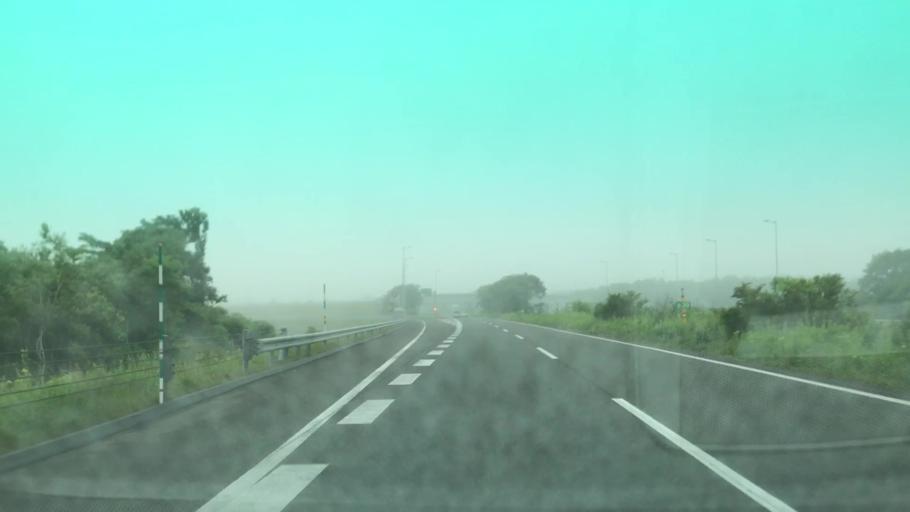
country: JP
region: Hokkaido
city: Chitose
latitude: 42.7796
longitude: 141.6272
